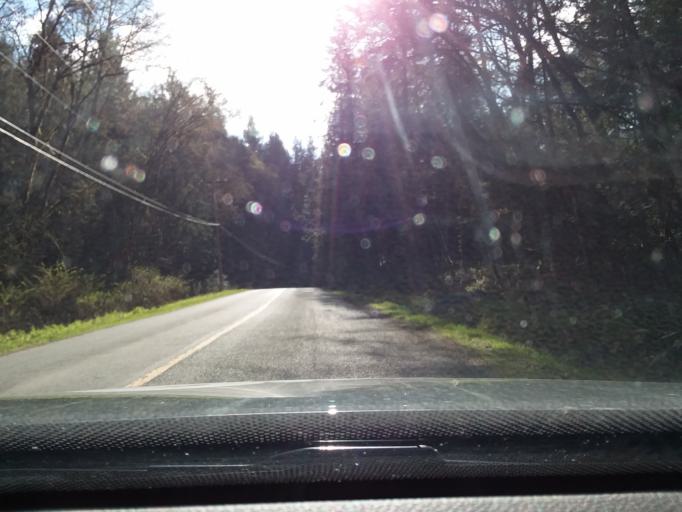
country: CA
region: British Columbia
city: North Cowichan
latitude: 48.9245
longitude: -123.4485
